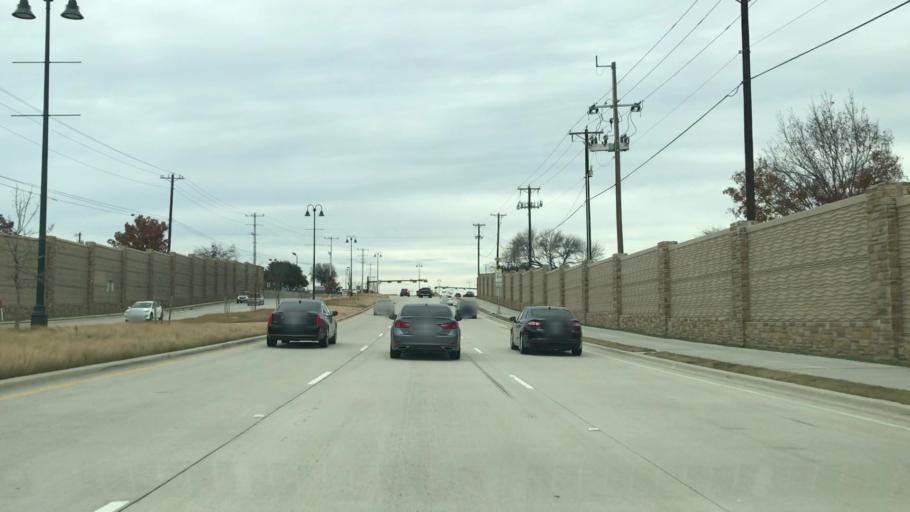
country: US
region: Texas
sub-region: Denton County
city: The Colony
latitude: 33.0935
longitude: -96.8925
